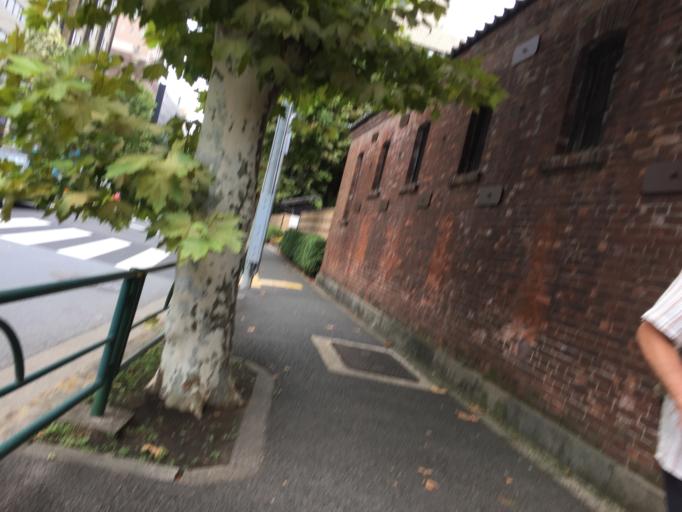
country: JP
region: Tokyo
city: Tokyo
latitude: 35.6682
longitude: 139.7273
